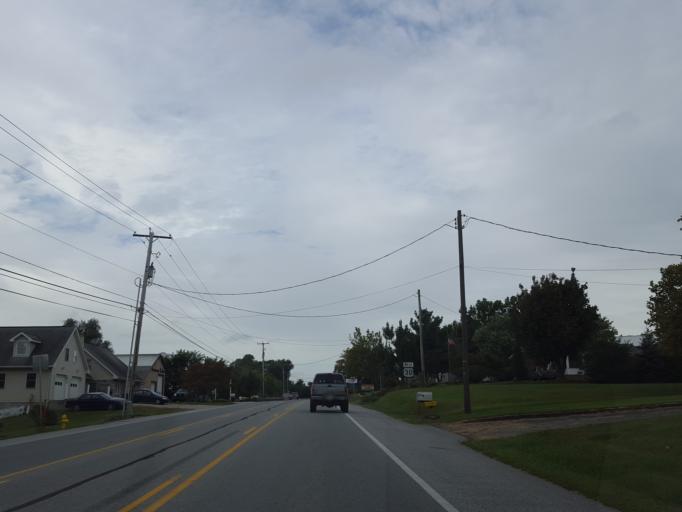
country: US
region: Pennsylvania
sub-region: Adams County
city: Abbottstown
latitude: 39.8988
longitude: -76.9515
